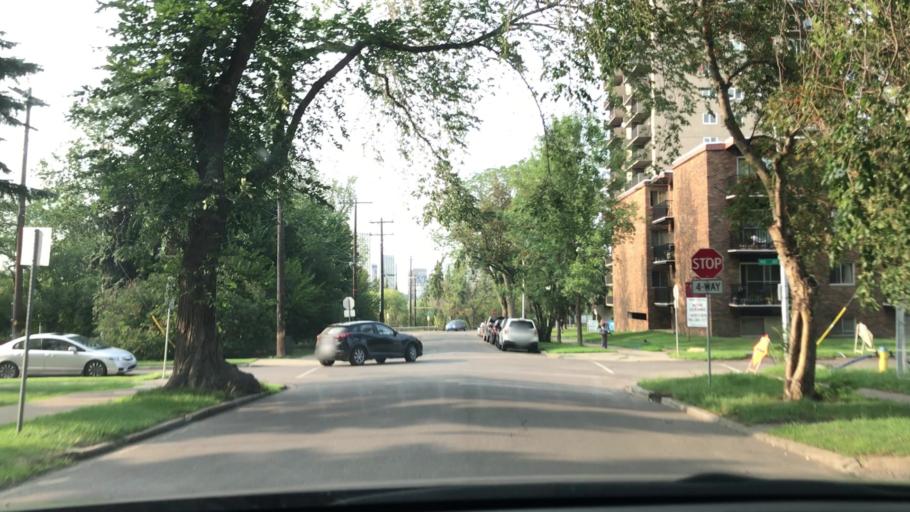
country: CA
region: Alberta
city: Edmonton
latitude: 53.5252
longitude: -113.4888
